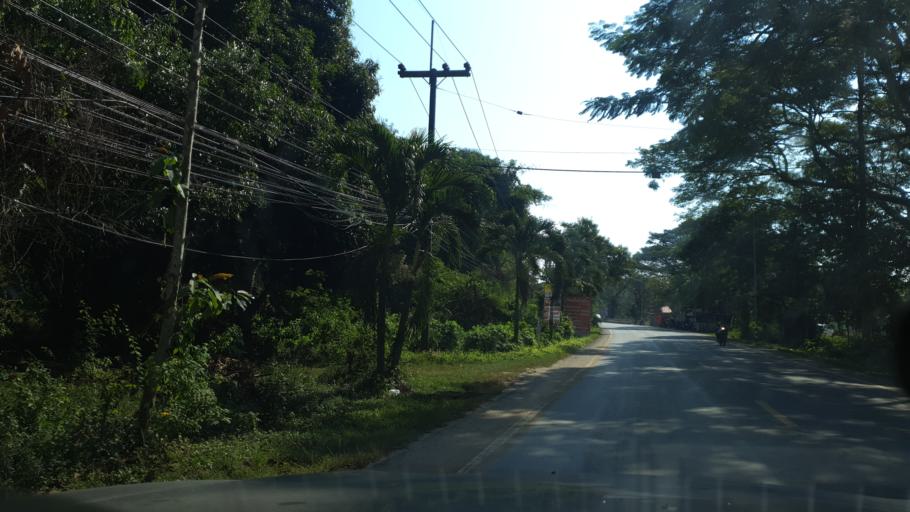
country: TH
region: Prachuap Khiri Khan
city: Bang Saphan
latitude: 11.3472
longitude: 99.5583
